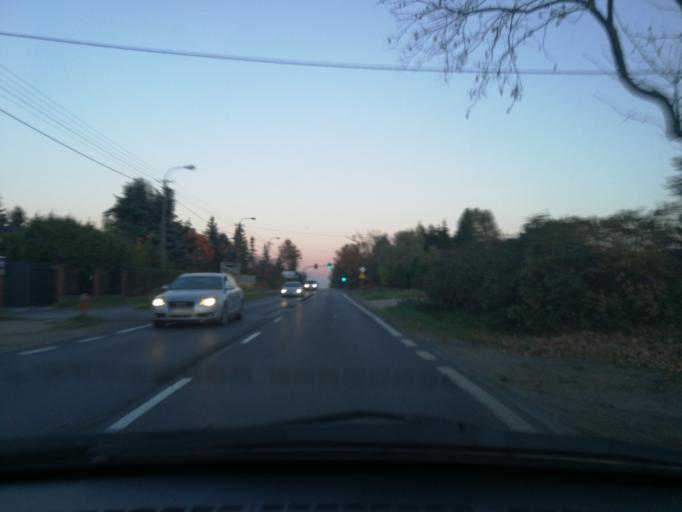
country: PL
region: Lodz Voivodeship
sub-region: Powiat lodzki wschodni
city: Andrespol
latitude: 51.7949
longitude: 19.5737
